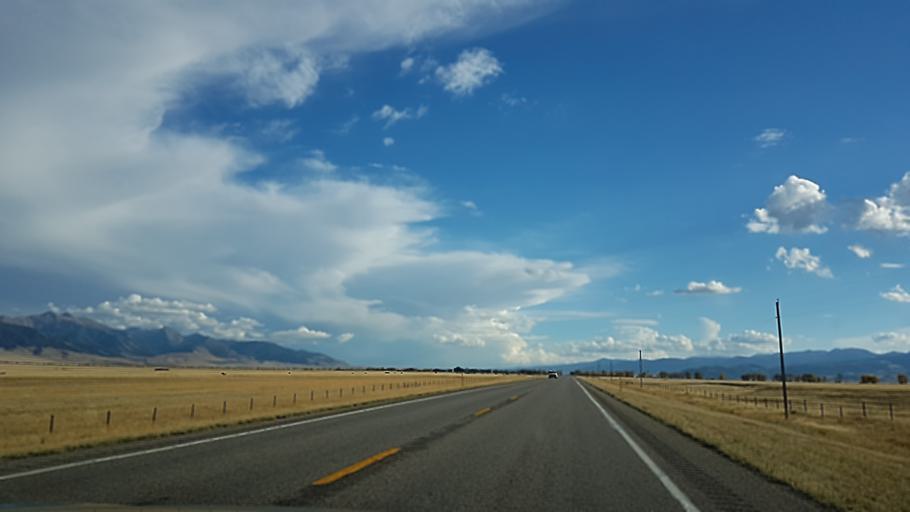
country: US
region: Montana
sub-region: Madison County
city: Virginia City
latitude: 45.2246
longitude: -111.6790
